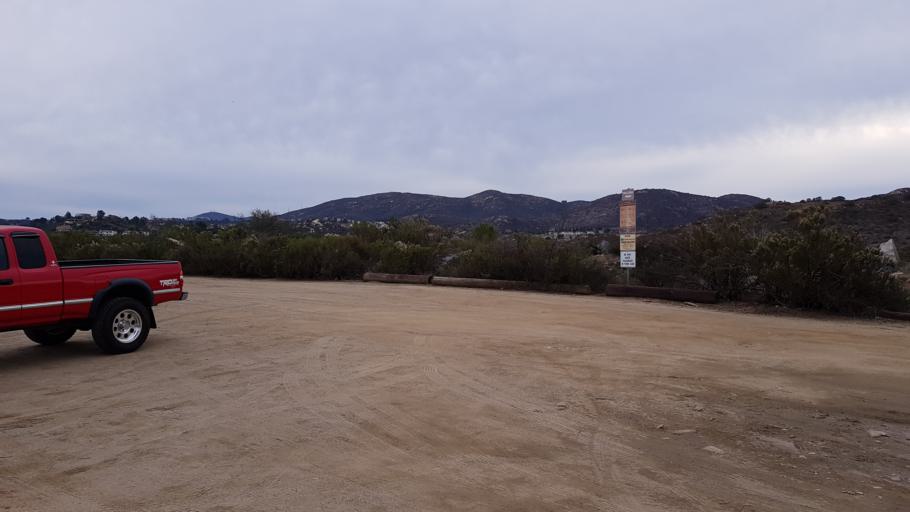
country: US
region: California
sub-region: San Diego County
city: Escondido
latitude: 33.0520
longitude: -117.0766
